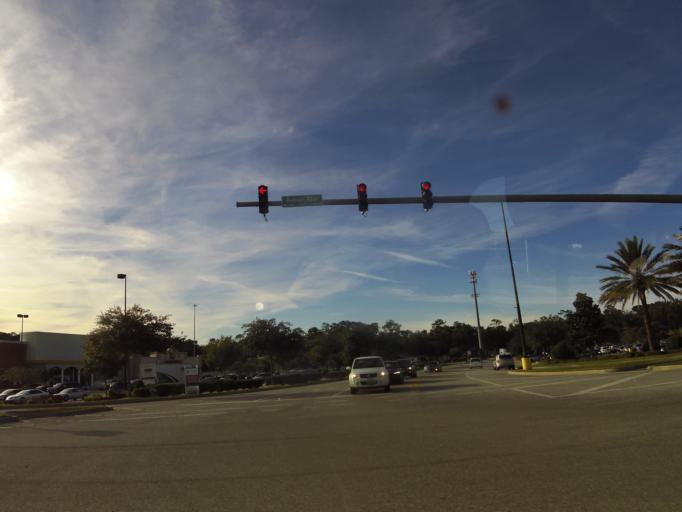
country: US
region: Florida
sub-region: Saint Johns County
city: Fruit Cove
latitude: 30.1770
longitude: -81.5562
